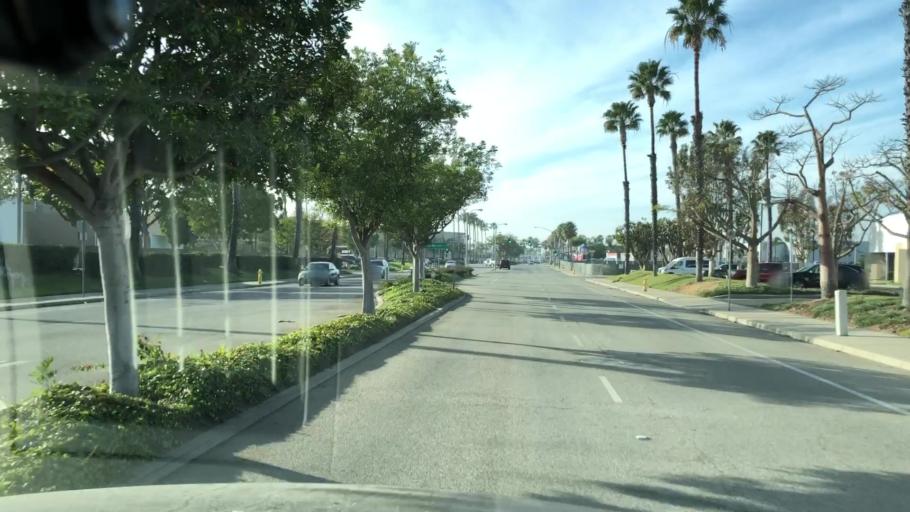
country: US
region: California
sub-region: Ventura County
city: El Rio
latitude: 34.2264
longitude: -119.1470
